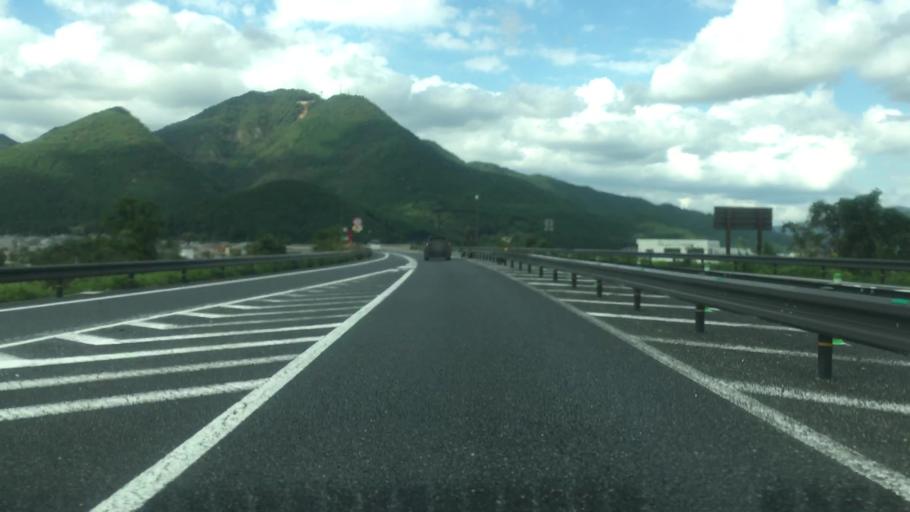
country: JP
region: Kyoto
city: Fukuchiyama
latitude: 35.1755
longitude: 135.0404
